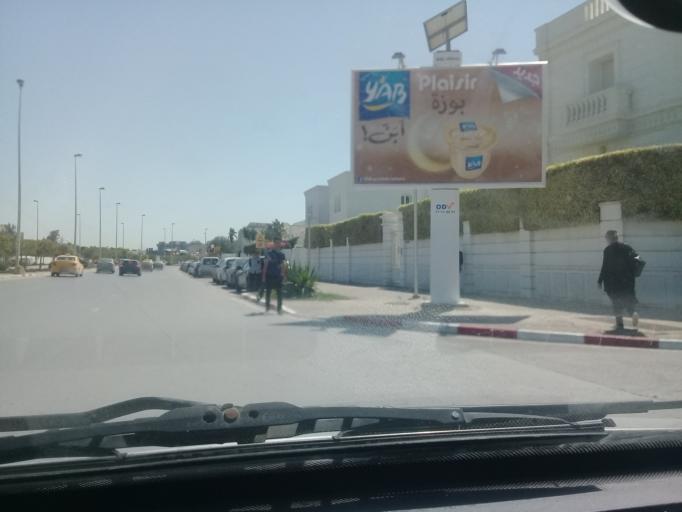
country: TN
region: Ariana
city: Ariana
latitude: 36.8388
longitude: 10.2464
